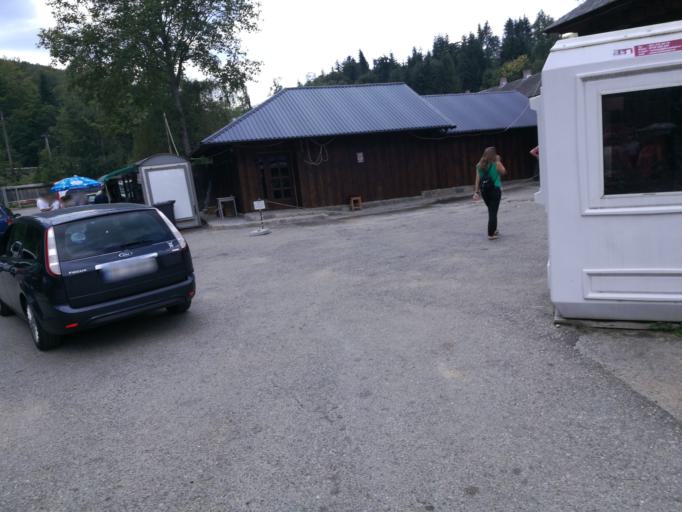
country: RO
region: Neamt
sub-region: Comuna Pipirig
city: Stanca
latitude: 47.1750
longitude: 26.1689
